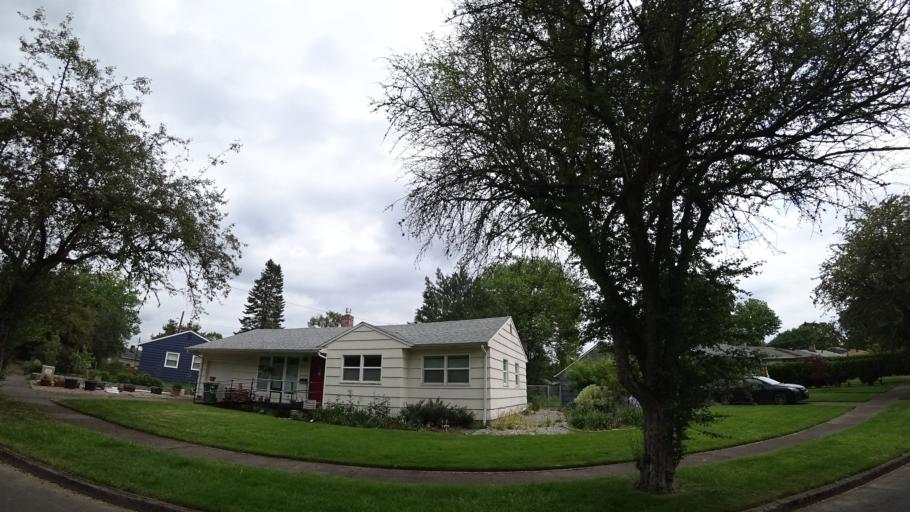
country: US
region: Oregon
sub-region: Washington County
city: Beaverton
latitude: 45.4858
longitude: -122.7913
